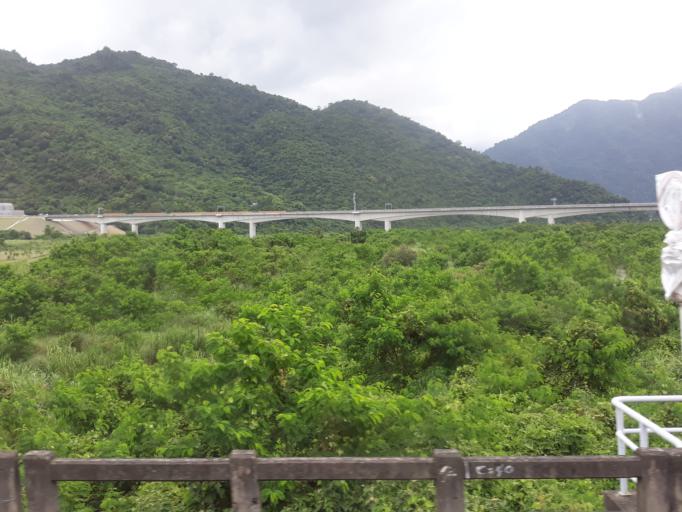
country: TW
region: Taiwan
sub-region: Yilan
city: Yilan
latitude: 24.4426
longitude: 121.7790
